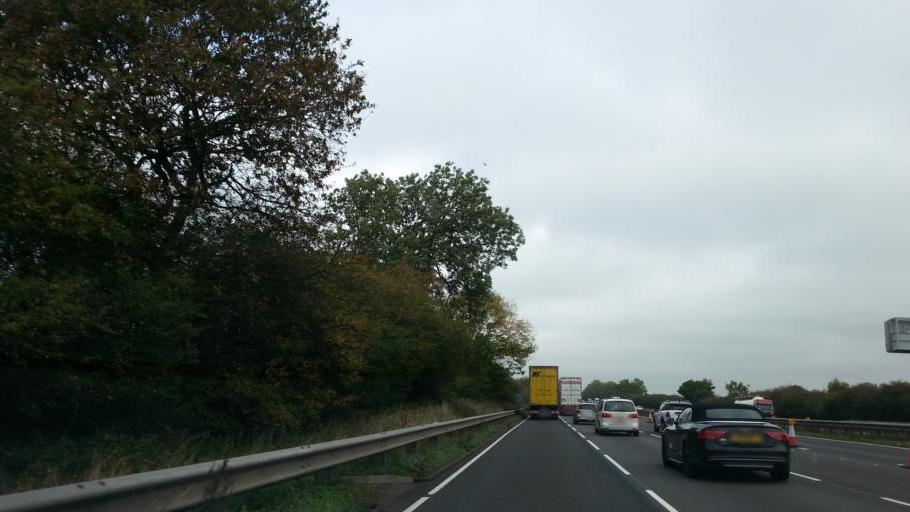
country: GB
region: England
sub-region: Staffordshire
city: Stone
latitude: 52.8559
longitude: -2.1619
